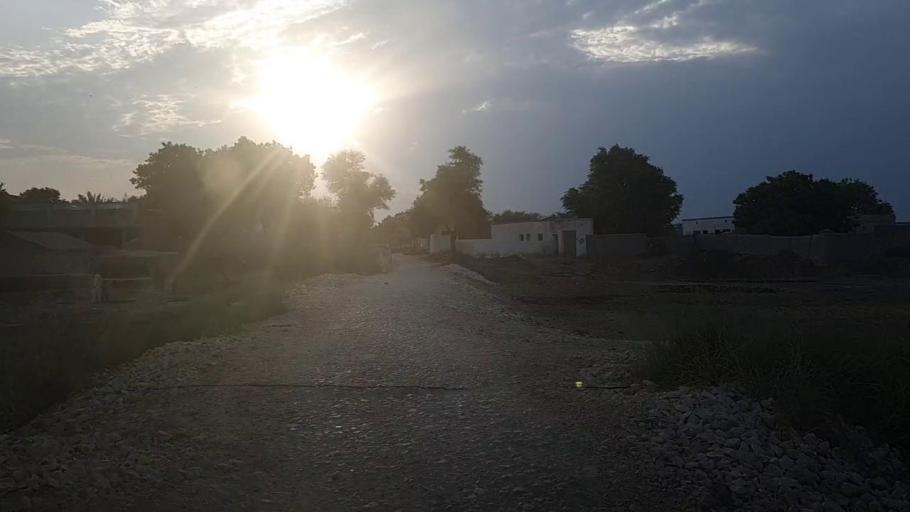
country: PK
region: Sindh
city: Ubauro
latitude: 28.3538
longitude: 69.7757
